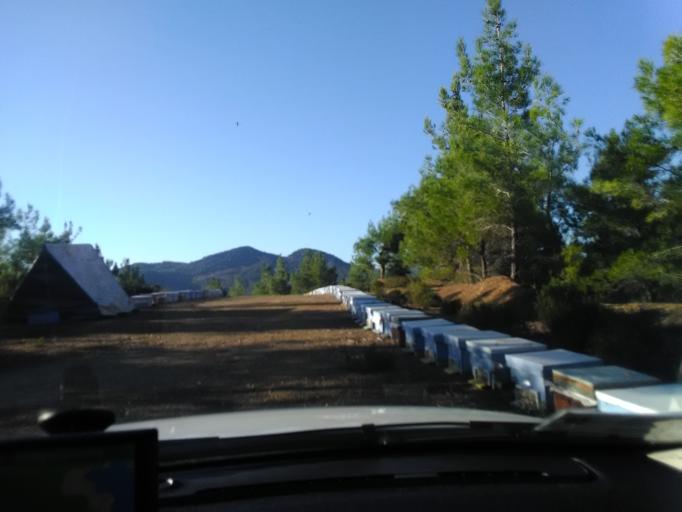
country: TR
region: Antalya
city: Gazipasa
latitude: 36.3090
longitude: 32.3939
